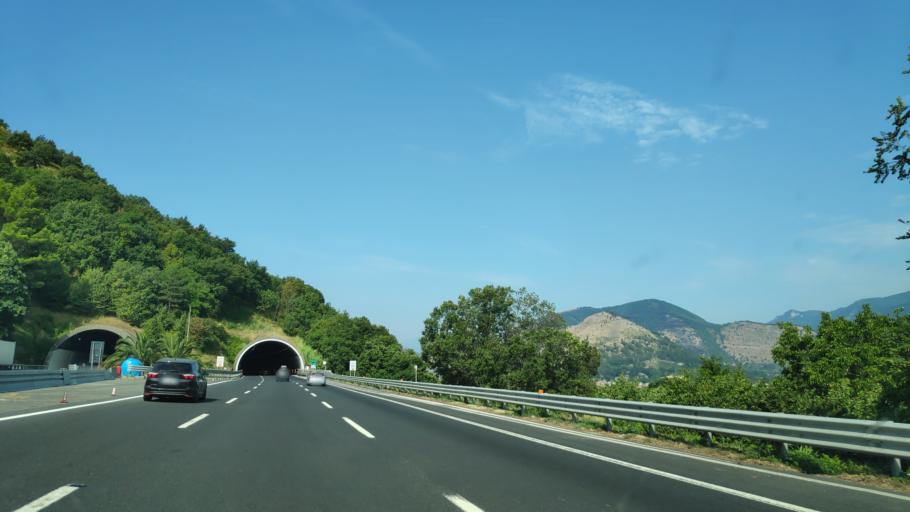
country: IT
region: Campania
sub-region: Provincia di Salerno
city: Piazza del Galdo-Sant'Angelo
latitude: 40.7727
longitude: 14.7208
